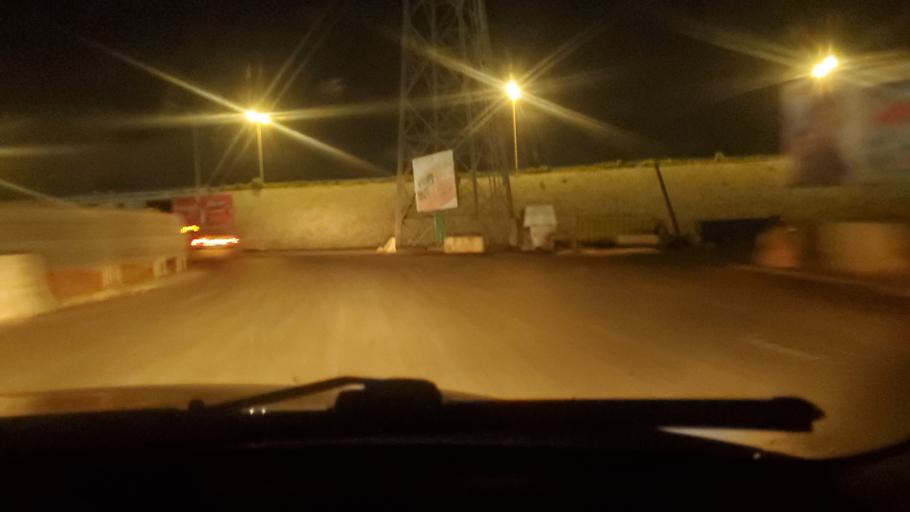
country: SN
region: Dakar
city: Pikine
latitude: 14.7431
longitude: -17.3945
